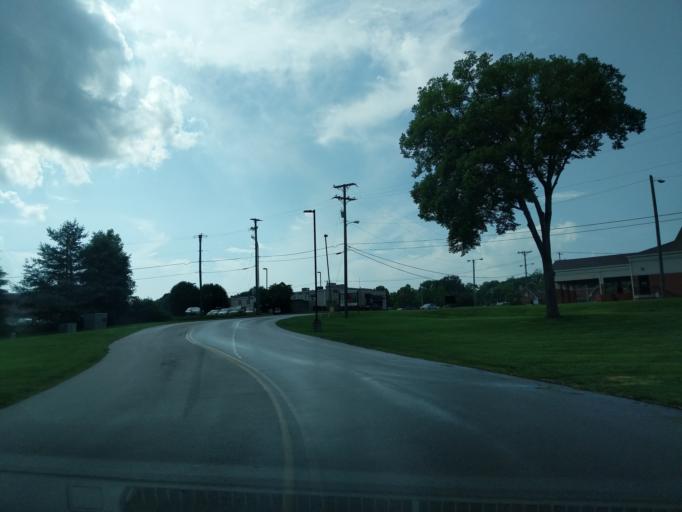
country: US
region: Tennessee
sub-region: Davidson County
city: Belle Meade
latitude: 36.0435
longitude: -86.9546
